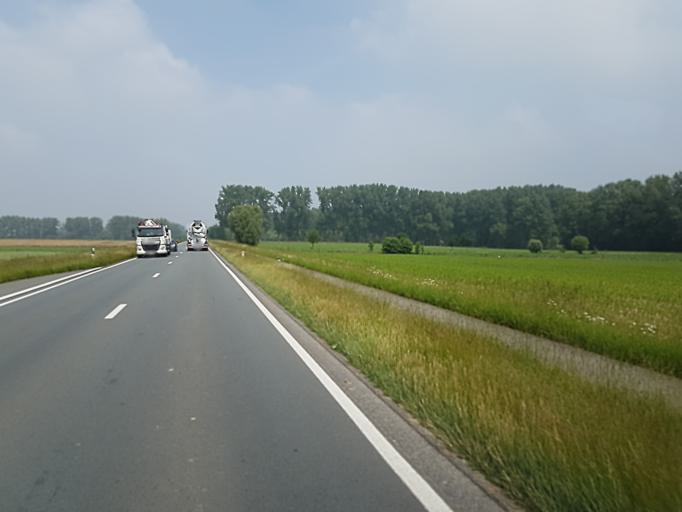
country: BE
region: Flanders
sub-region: Provincie Oost-Vlaanderen
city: Sint-Maria-Lierde
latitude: 50.8256
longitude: 3.8687
